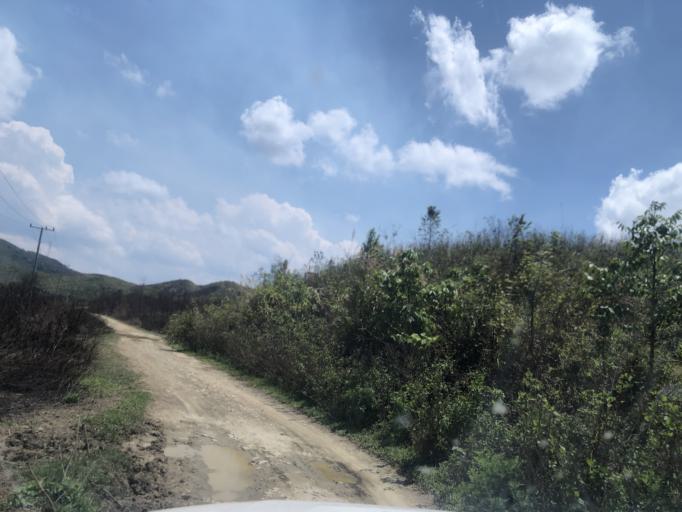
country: LA
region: Phongsali
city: Phongsali
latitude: 21.4088
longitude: 102.1864
